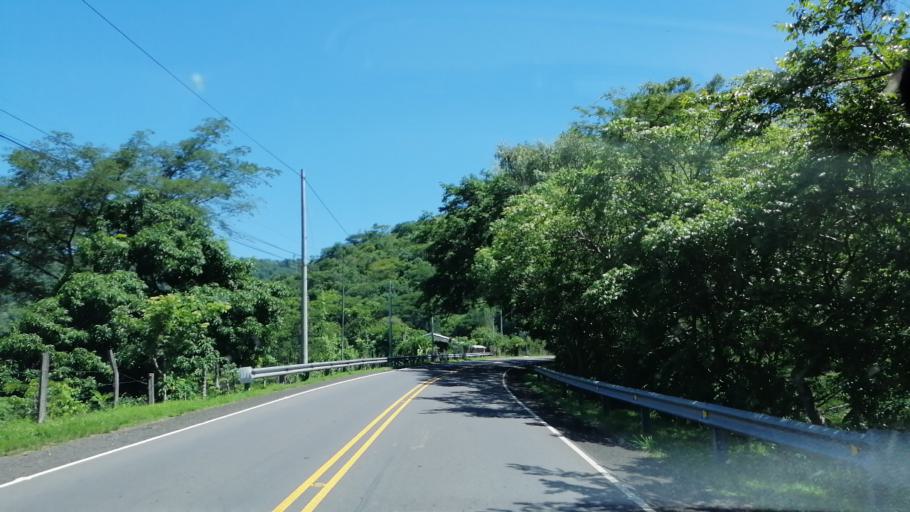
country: SV
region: Morazan
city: Cacaopera
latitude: 13.8015
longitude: -88.1468
